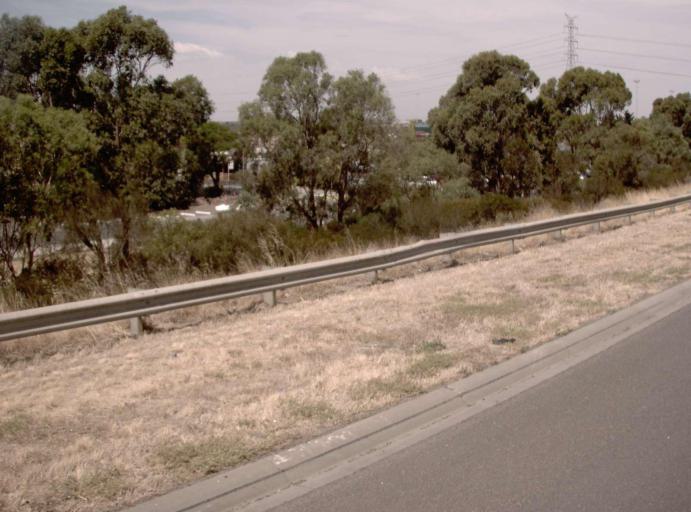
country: AU
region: Victoria
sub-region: Brimbank
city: Brooklyn
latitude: -37.8234
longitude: 144.8115
